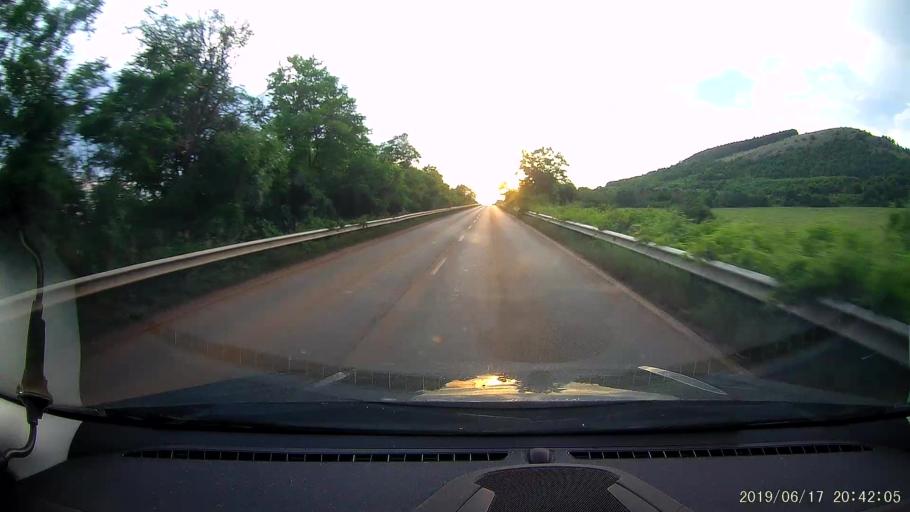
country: BG
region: Sofiya
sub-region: Obshtina Dragoman
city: Dragoman
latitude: 42.8998
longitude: 22.9565
